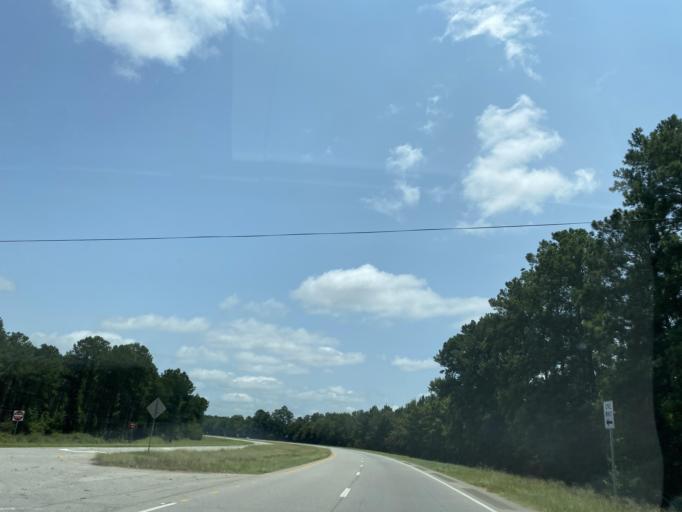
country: US
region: Georgia
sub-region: Telfair County
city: Lumber City
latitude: 31.9091
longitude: -82.6675
